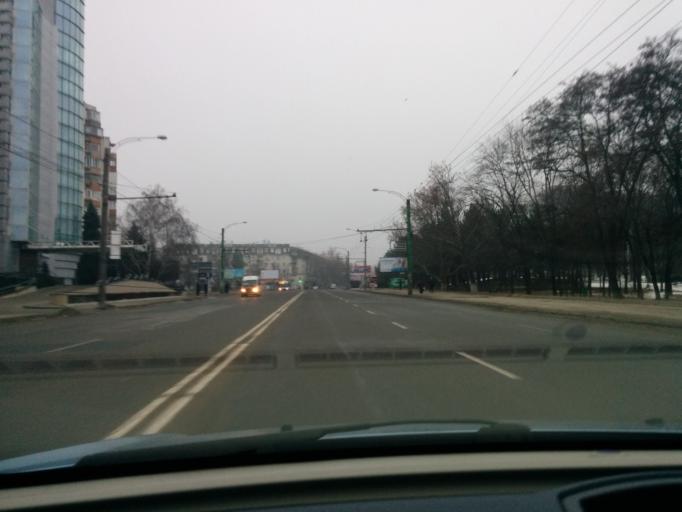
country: MD
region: Chisinau
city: Chisinau
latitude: 47.0029
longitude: 28.8598
